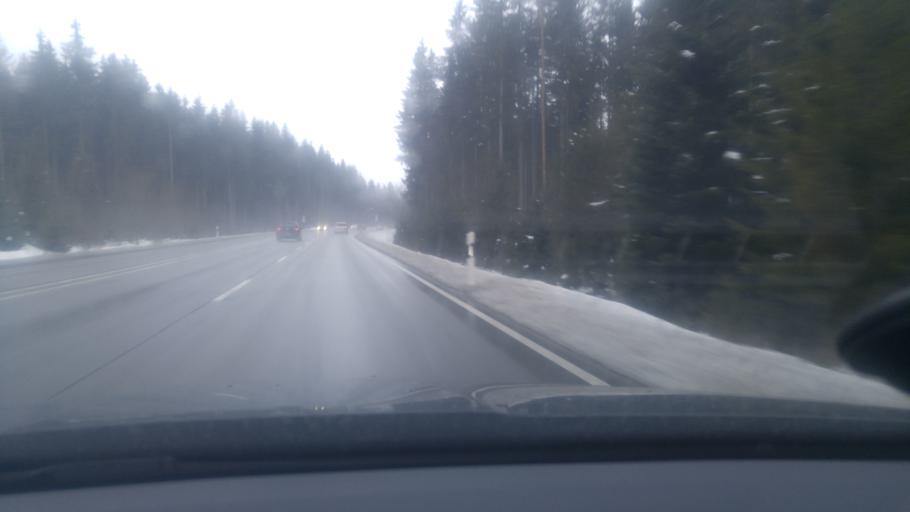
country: DE
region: Baden-Wuerttemberg
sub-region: Freiburg Region
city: Friedenweiler
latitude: 47.8990
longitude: 8.2710
